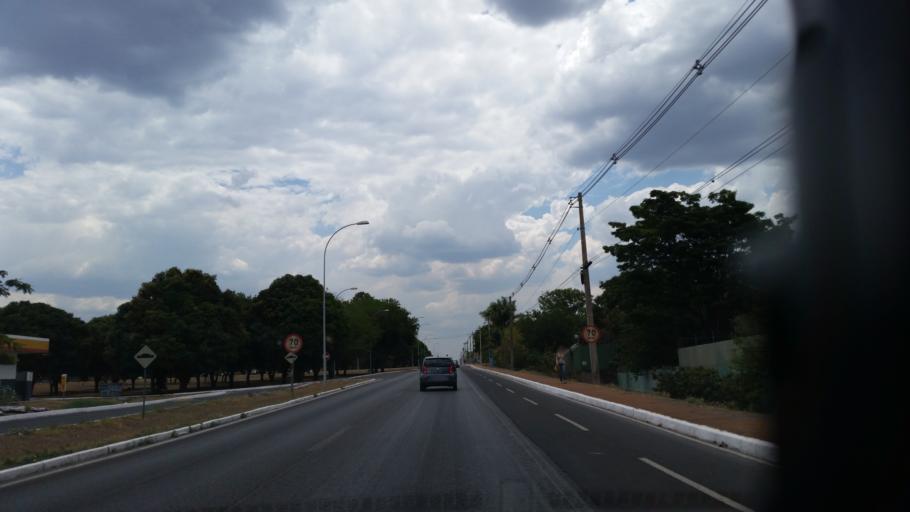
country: BR
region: Federal District
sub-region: Brasilia
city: Brasilia
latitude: -15.7272
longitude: -47.8717
